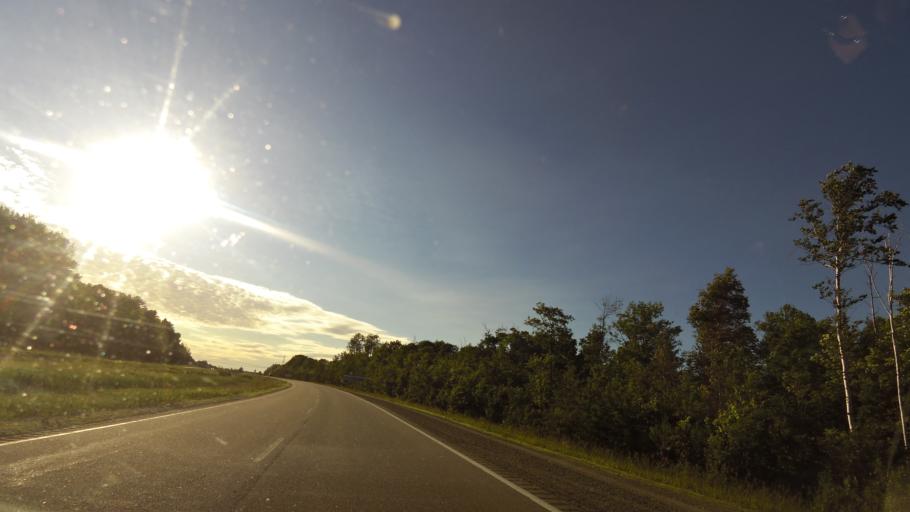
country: CA
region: Ontario
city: Midland
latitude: 44.7386
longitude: -79.6865
